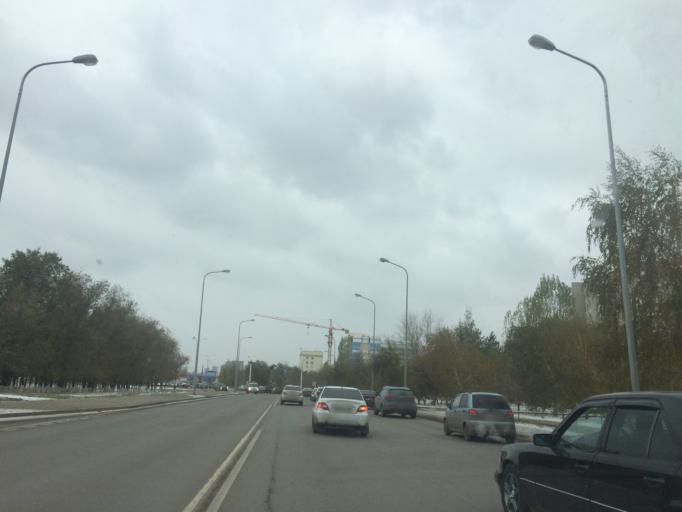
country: KZ
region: Astana Qalasy
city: Astana
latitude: 51.1623
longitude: 71.4699
